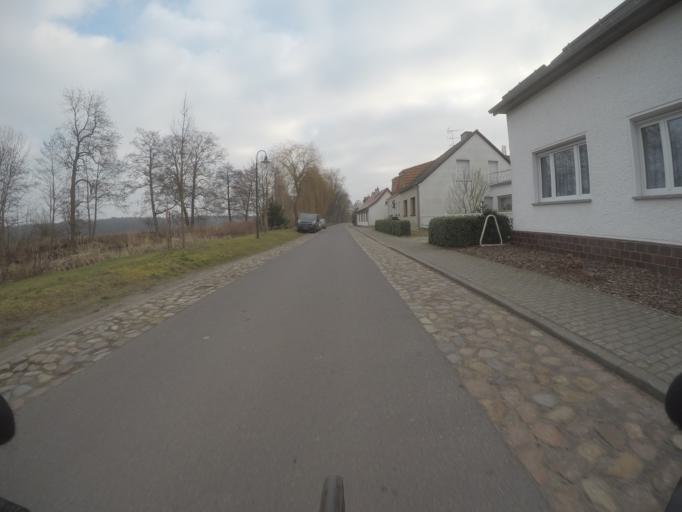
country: DE
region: Brandenburg
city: Marienwerder
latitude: 52.8563
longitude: 13.5107
